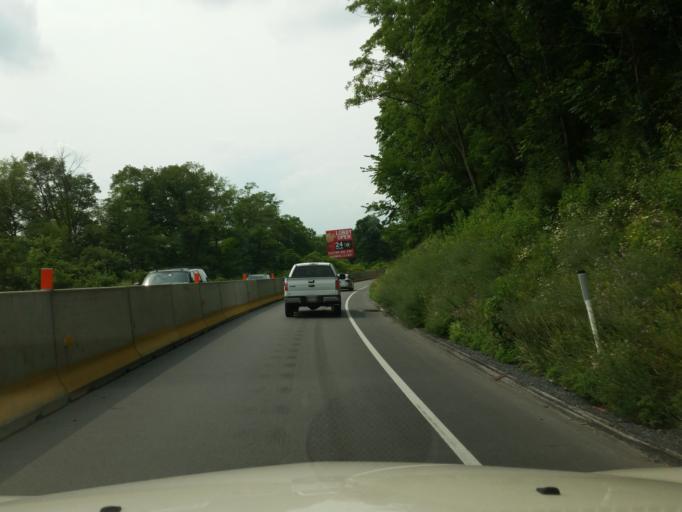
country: US
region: Pennsylvania
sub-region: Mifflin County
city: Lewistown
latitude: 40.5797
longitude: -77.5521
